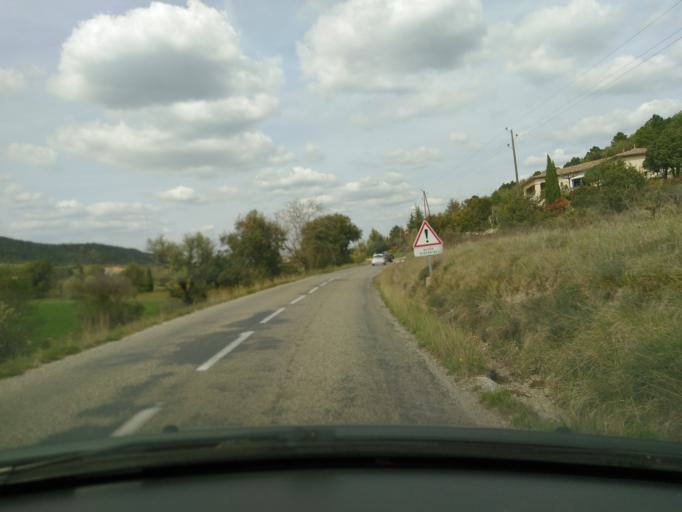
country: FR
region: Rhone-Alpes
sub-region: Departement de l'Ardeche
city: Ruoms
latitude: 44.4370
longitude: 4.4107
